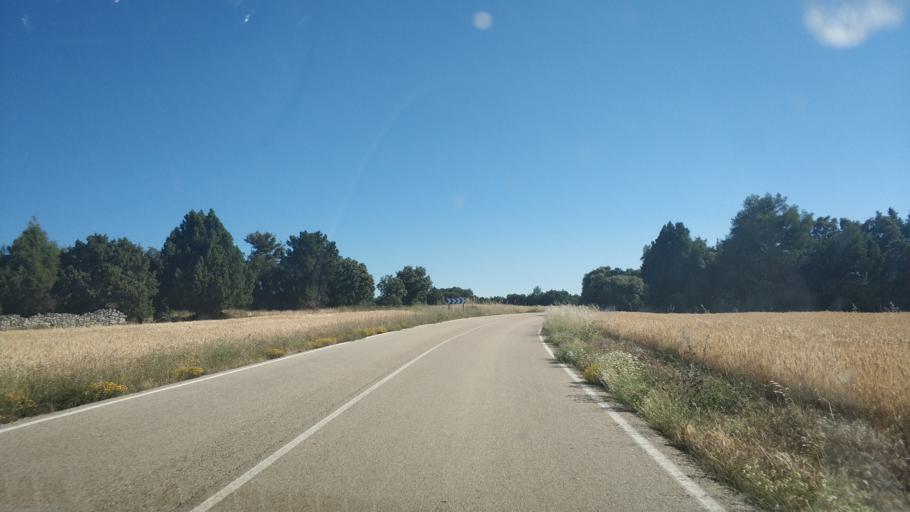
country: ES
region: Castille and Leon
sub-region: Provincia de Soria
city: Liceras
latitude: 41.4539
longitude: -3.2124
